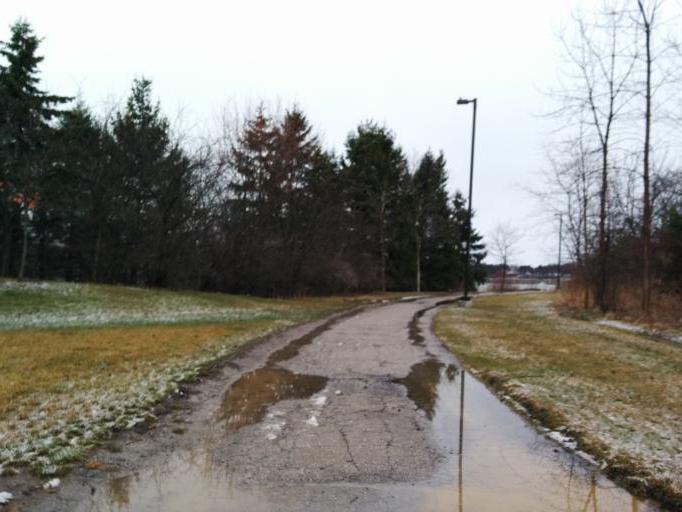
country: CA
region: Ontario
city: Etobicoke
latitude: 43.5643
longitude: -79.5638
